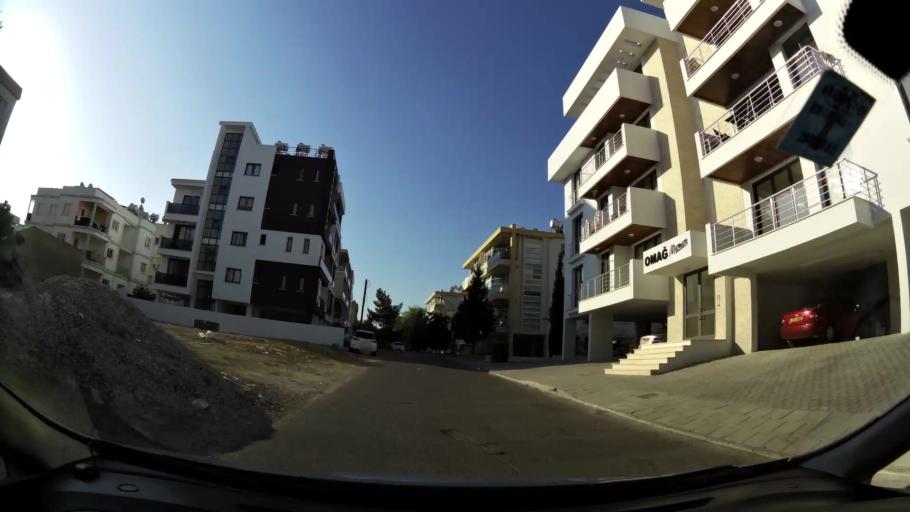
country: CY
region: Lefkosia
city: Nicosia
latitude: 35.2031
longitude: 33.3467
